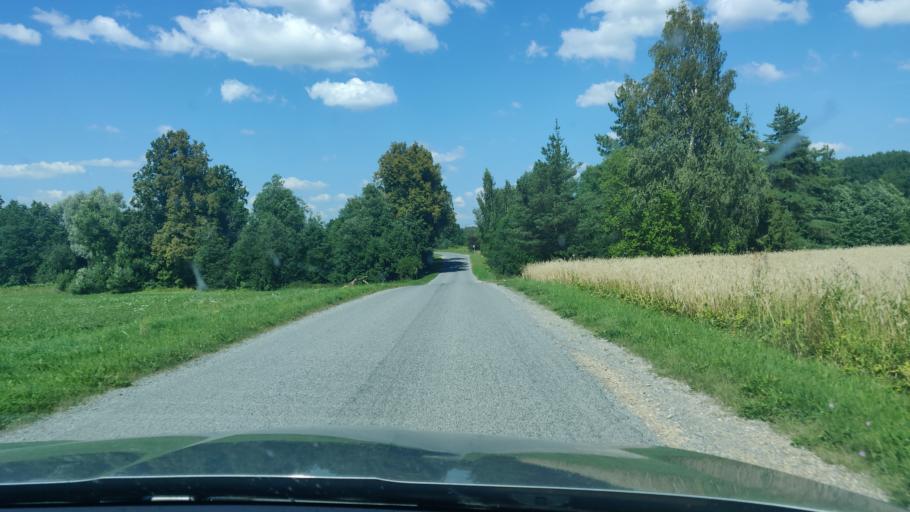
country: EE
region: Tartu
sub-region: Elva linn
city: Elva
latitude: 58.1589
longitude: 26.4703
